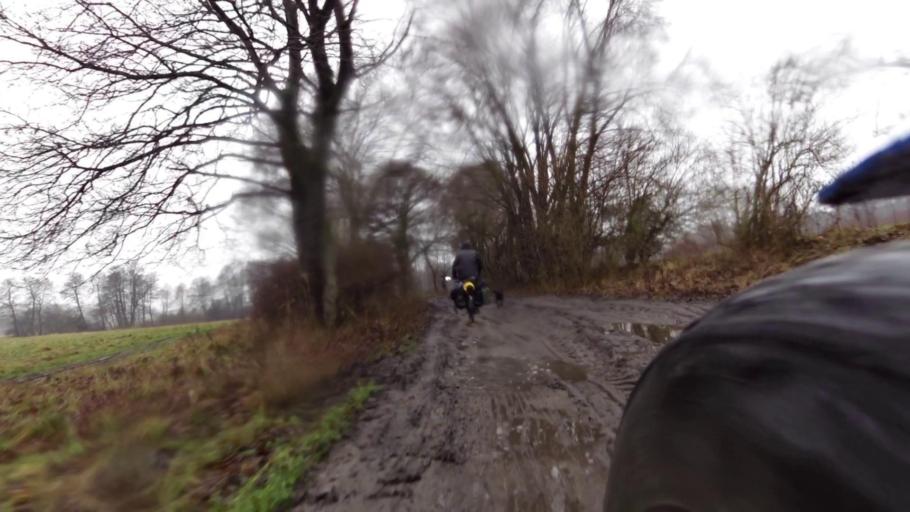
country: PL
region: West Pomeranian Voivodeship
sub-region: Powiat drawski
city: Zlocieniec
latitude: 53.5485
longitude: 15.9422
